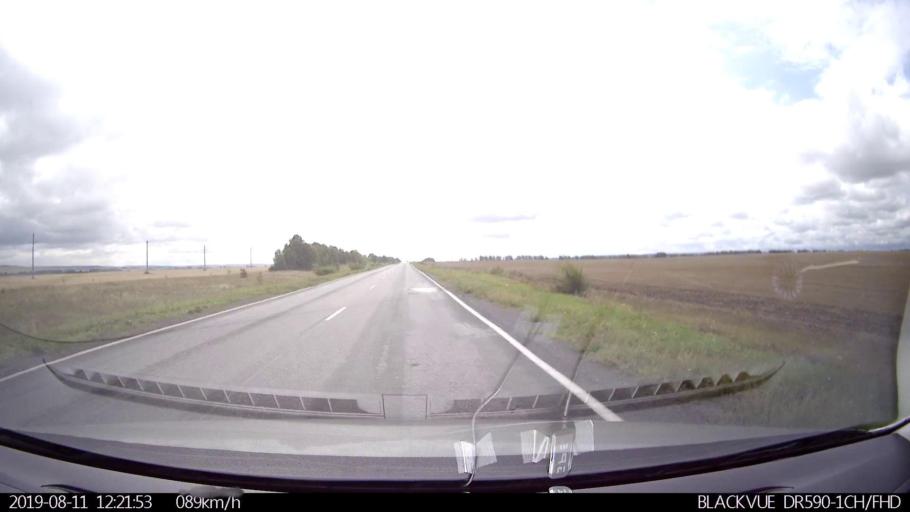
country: RU
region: Ulyanovsk
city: Ignatovka
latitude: 53.9153
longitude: 47.9562
